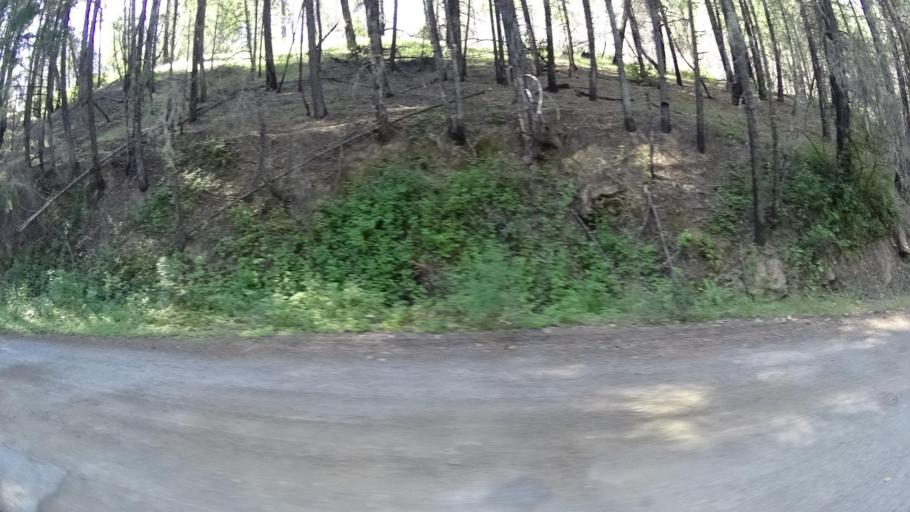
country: US
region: California
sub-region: Lake County
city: Upper Lake
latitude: 39.4079
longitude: -122.9815
